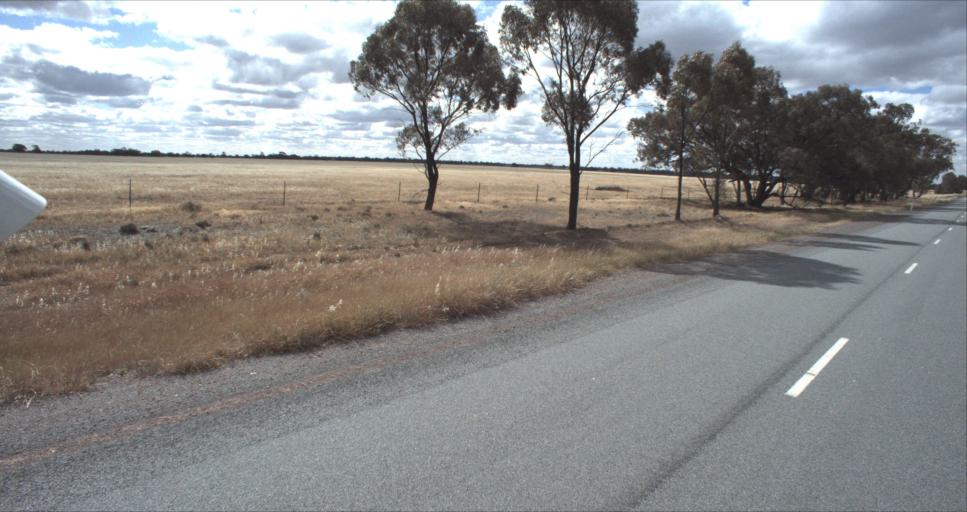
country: AU
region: New South Wales
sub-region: Leeton
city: Leeton
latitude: -34.6787
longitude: 146.3460
